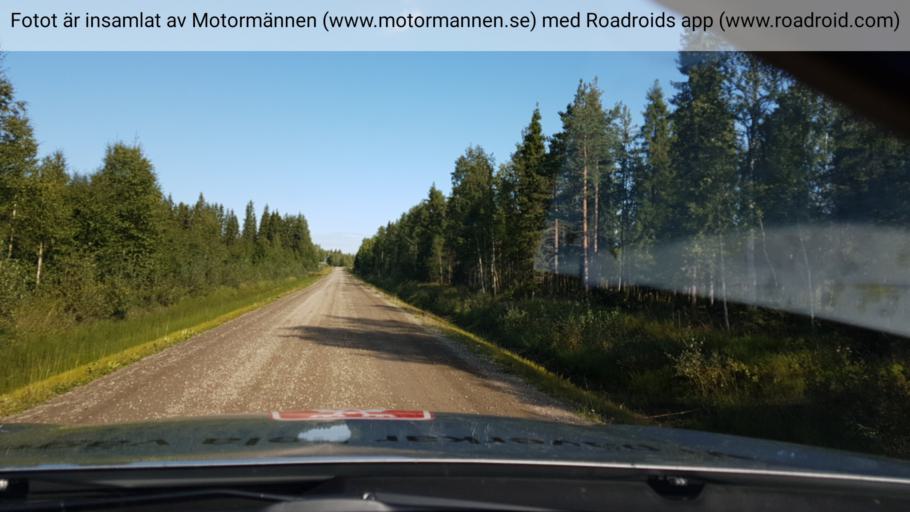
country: SE
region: Norrbotten
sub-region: Kalix Kommun
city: Kalix
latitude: 66.1874
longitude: 23.1982
